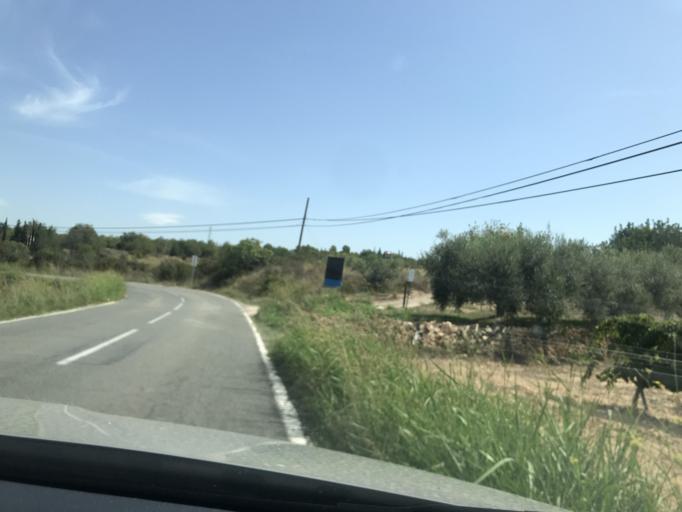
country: ES
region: Catalonia
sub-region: Provincia de Tarragona
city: Altafulla
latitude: 41.1732
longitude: 1.3721
